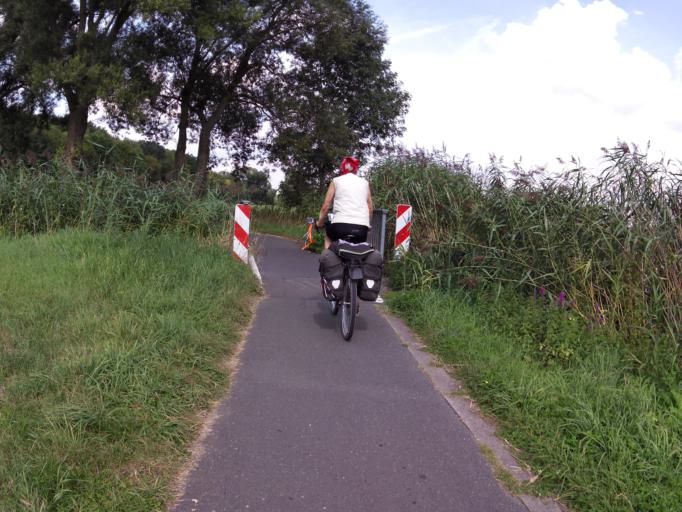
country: DE
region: North Rhine-Westphalia
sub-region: Regierungsbezirk Detmold
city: Petershagen
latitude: 52.3438
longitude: 8.9460
